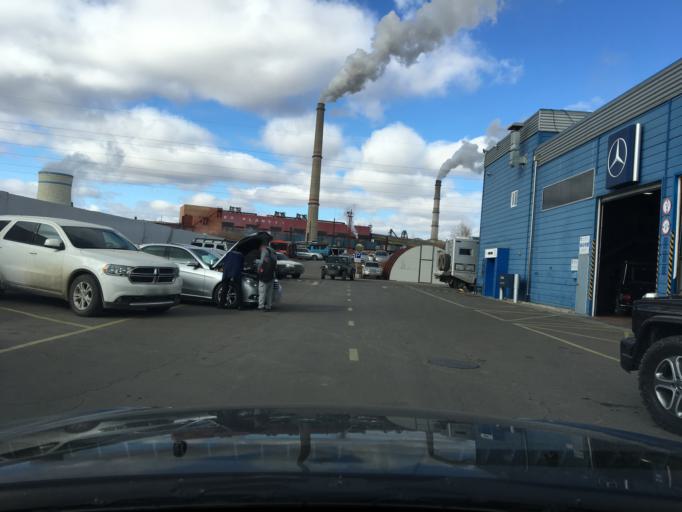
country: MN
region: Ulaanbaatar
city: Ulaanbaatar
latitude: 47.8913
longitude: 106.8687
